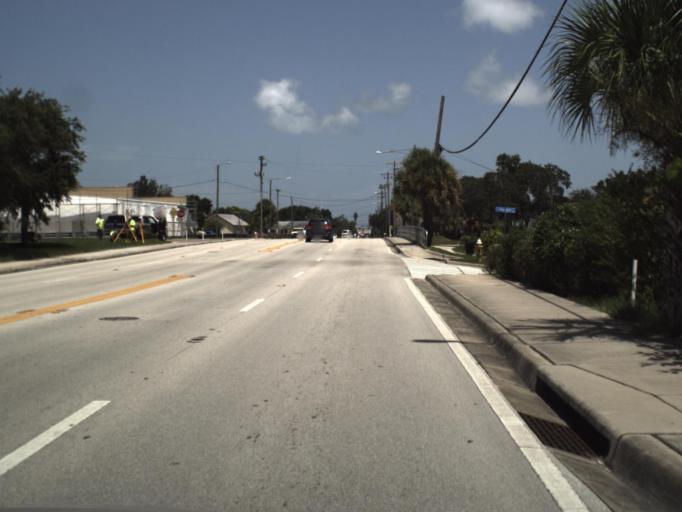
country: US
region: Florida
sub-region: Pinellas County
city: Clearwater
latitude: 27.9765
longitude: -82.7959
